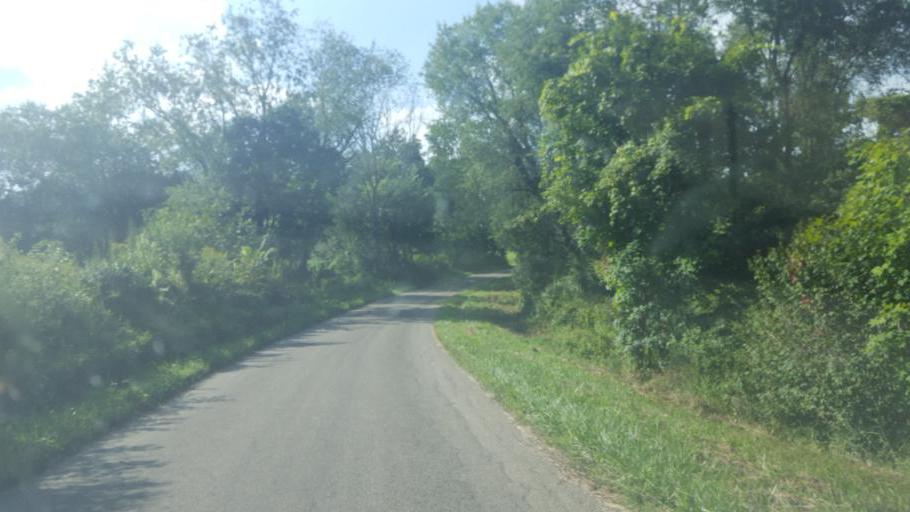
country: US
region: Ohio
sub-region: Knox County
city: Danville
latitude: 40.4849
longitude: -82.3110
